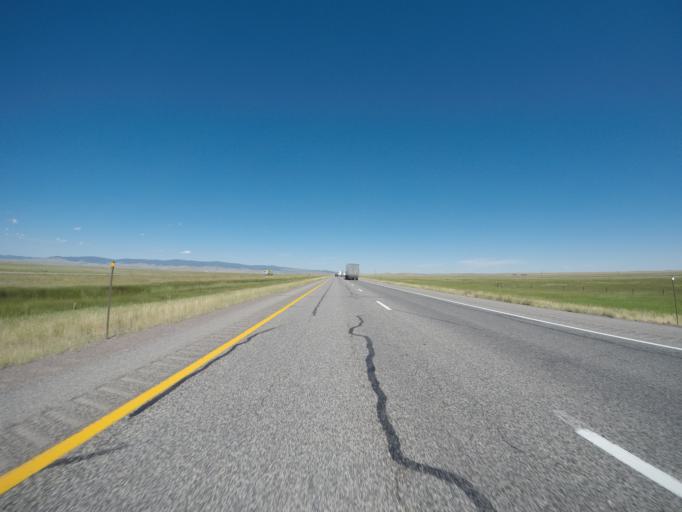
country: US
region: Wyoming
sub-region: Albany County
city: Laramie
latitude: 41.4171
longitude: -105.8533
